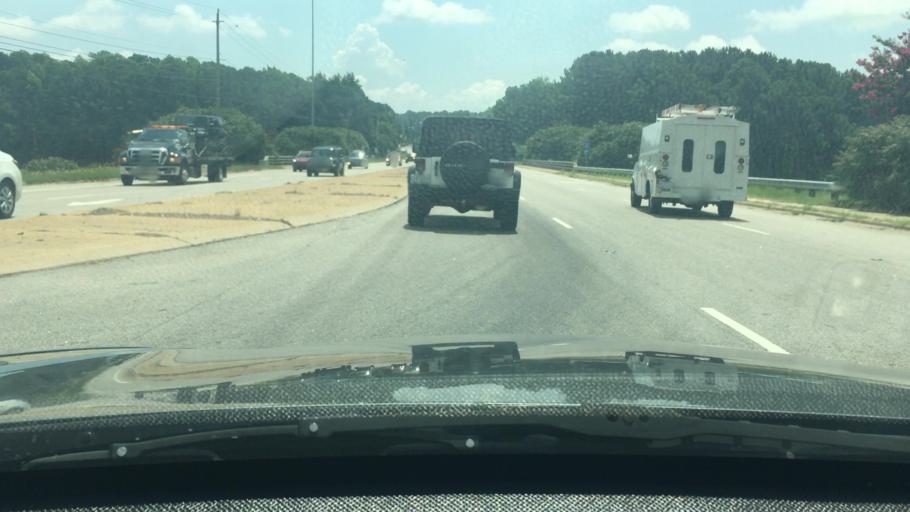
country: US
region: North Carolina
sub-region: Wake County
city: Cary
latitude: 35.7927
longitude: -78.7466
